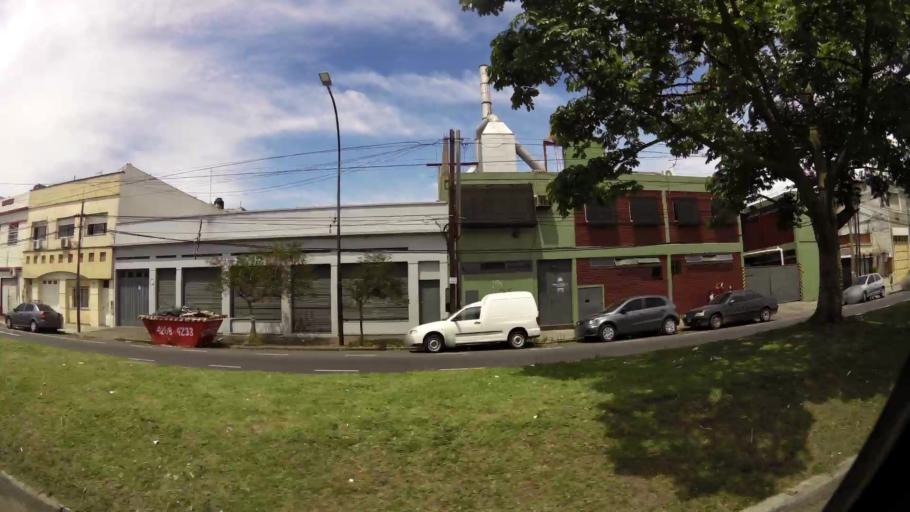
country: AR
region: Buenos Aires
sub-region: Partido de Lanus
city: Lanus
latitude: -34.6749
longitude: -58.3975
